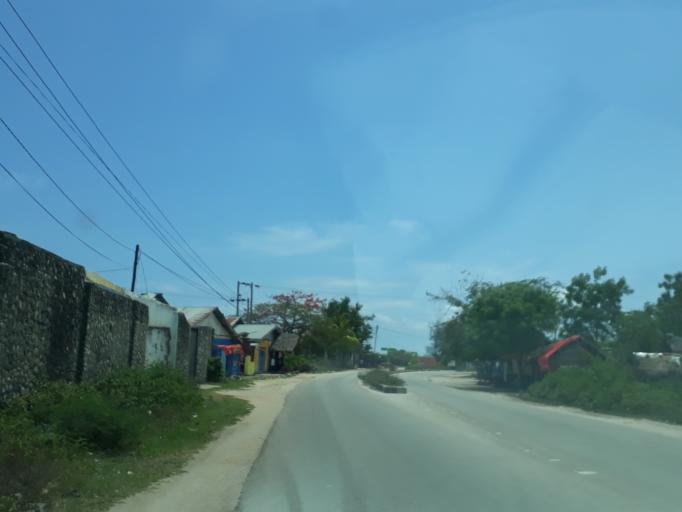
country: TZ
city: Kiwengwa
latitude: -5.9903
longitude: 39.3747
